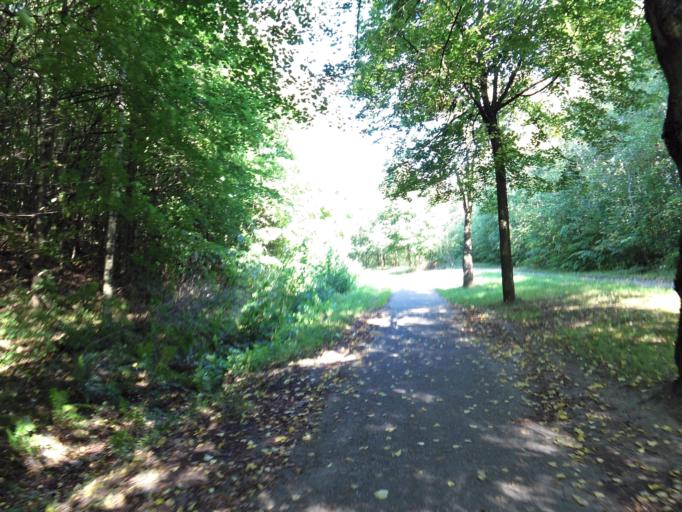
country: NL
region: Limburg
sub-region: Gemeente Kerkrade
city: Kerkrade
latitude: 50.8770
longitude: 6.0286
